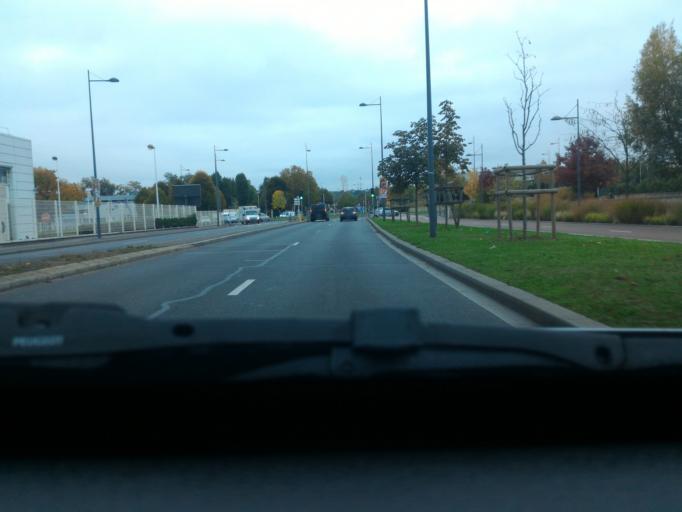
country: FR
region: Ile-de-France
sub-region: Departement du Val-de-Marne
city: Bonneuil-sur-Marne
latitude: 48.7733
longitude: 2.4933
